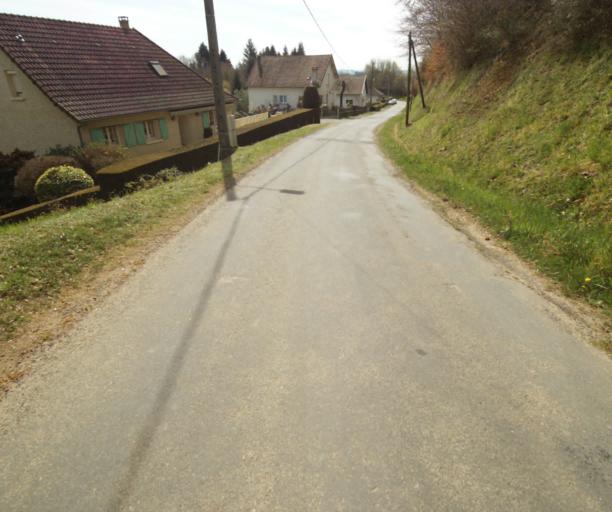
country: FR
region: Limousin
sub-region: Departement de la Correze
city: Naves
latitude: 45.3302
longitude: 1.7693
